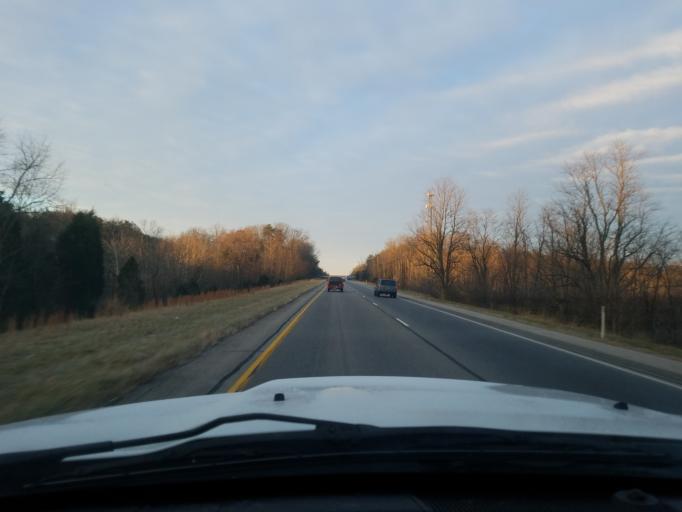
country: US
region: Indiana
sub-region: Floyd County
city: Georgetown
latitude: 38.2804
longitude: -85.9490
